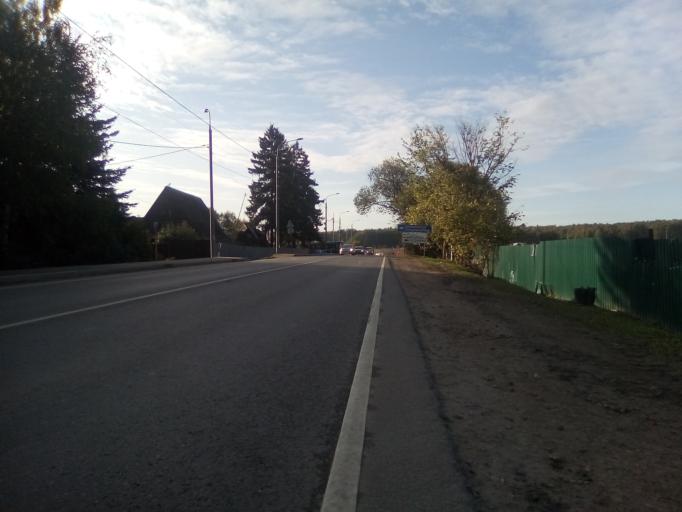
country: RU
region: Moskovskaya
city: Filimonki
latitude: 55.5570
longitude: 37.3343
